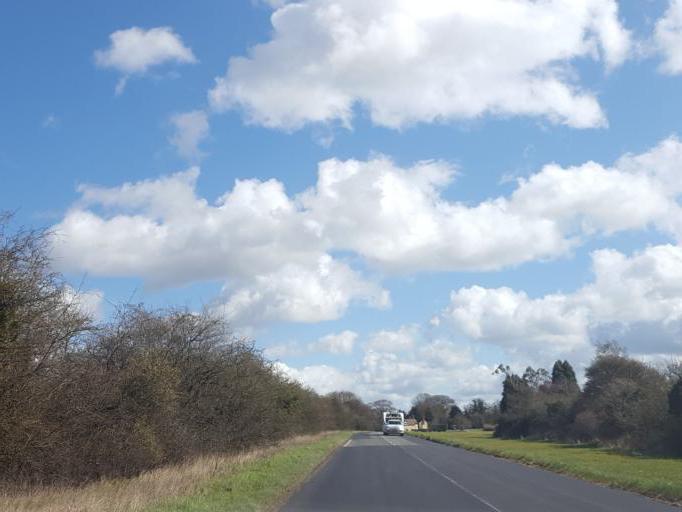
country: GB
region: England
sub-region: Worcestershire
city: Kempsey
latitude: 52.1046
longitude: -2.2489
